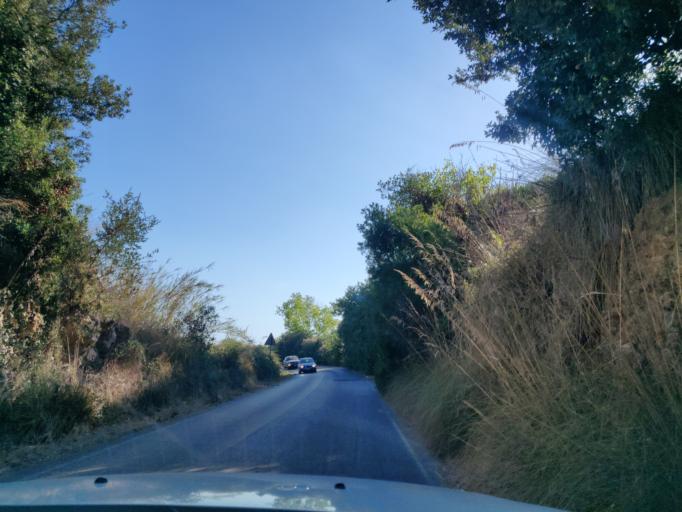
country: IT
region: Tuscany
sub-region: Provincia di Grosseto
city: Orbetello Scalo
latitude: 42.4271
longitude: 11.2822
